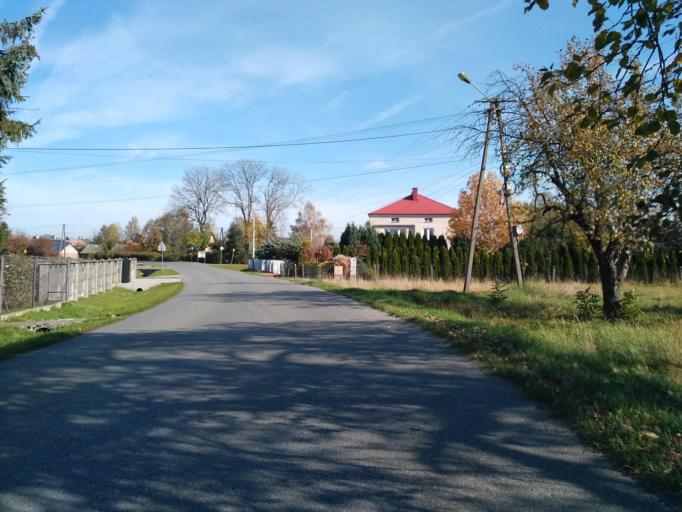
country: PL
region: Subcarpathian Voivodeship
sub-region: Powiat rzeszowski
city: Trzciana
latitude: 50.0752
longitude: 21.7995
